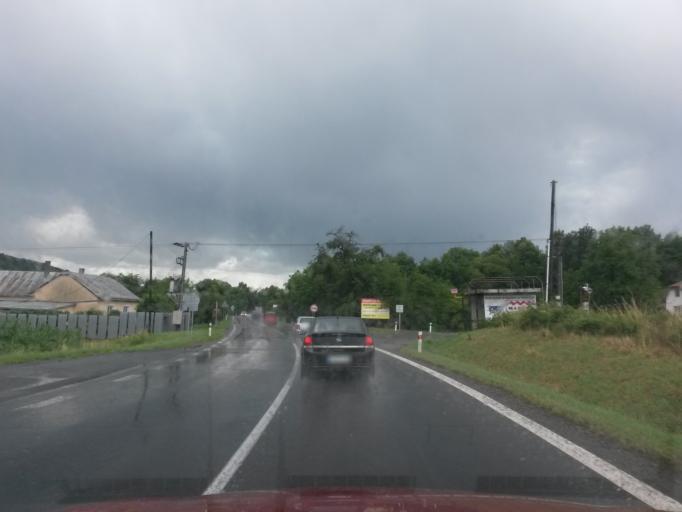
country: SK
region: Presovsky
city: Vranov nad Topl'ou
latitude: 48.9689
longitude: 21.5799
